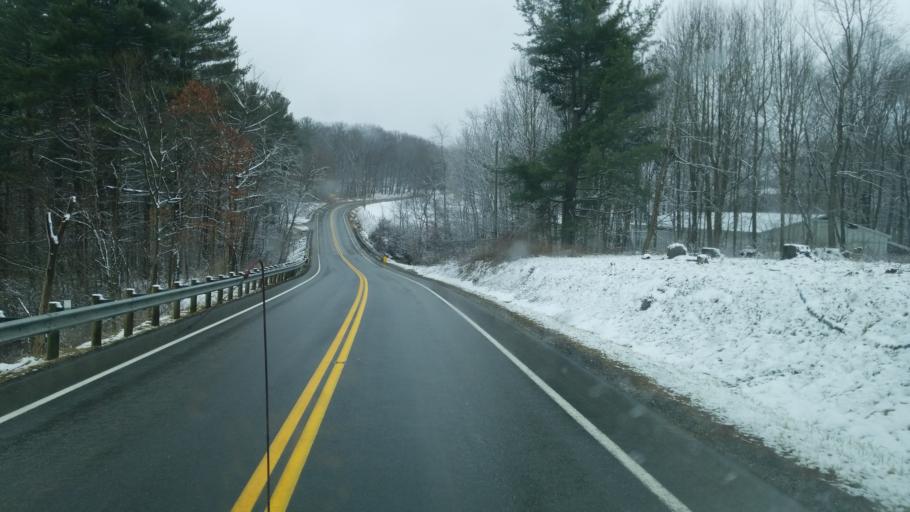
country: US
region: Ohio
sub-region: Geauga County
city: Middlefield
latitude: 41.3825
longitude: -81.0764
